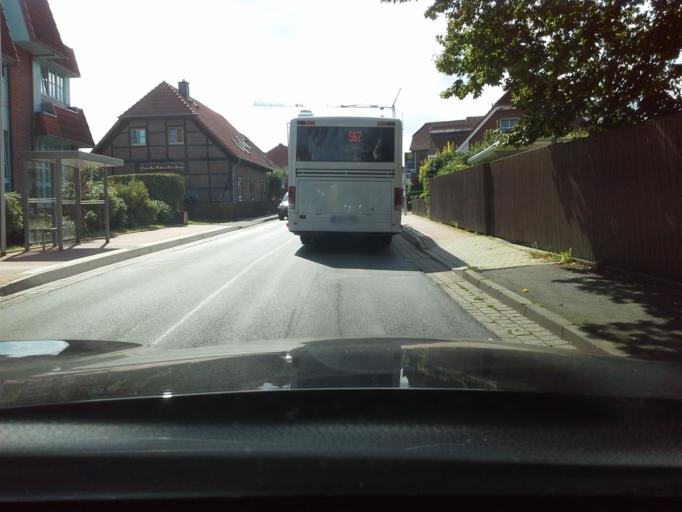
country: DE
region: Lower Saxony
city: Egestorf
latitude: 52.2880
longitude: 9.5150
